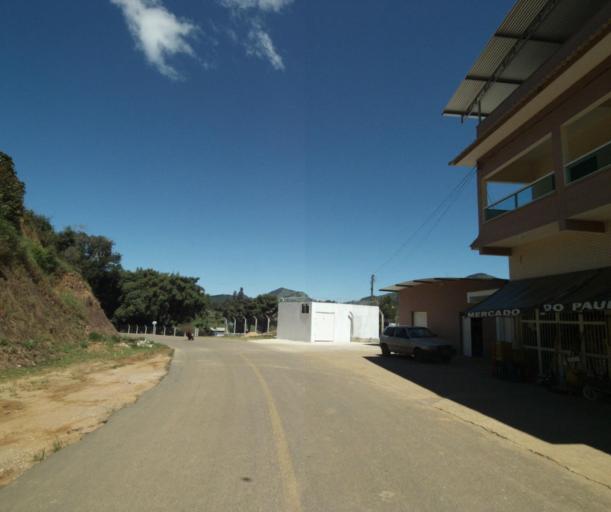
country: BR
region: Minas Gerais
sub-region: Espera Feliz
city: Espera Feliz
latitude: -20.5649
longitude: -41.8279
